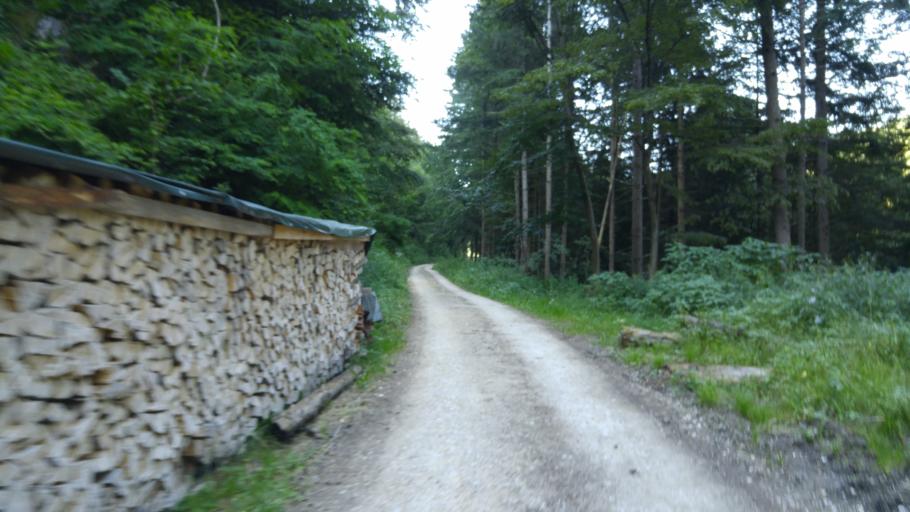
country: DE
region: Baden-Wuerttemberg
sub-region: Freiburg Region
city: Muenstertal/Schwarzwald
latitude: 47.8376
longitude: 7.7873
